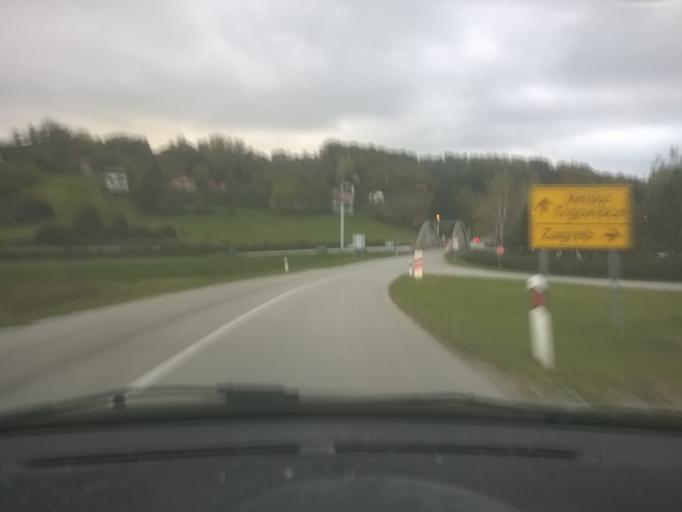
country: HR
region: Zagrebacka
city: Jakovlje
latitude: 45.9752
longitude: 15.8472
